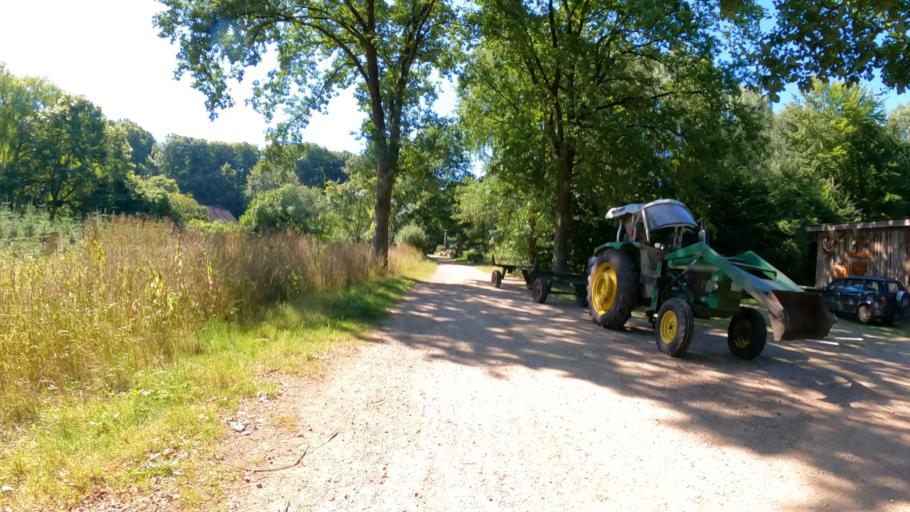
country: DE
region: Schleswig-Holstein
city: Kroppelshagen-Fahrendorf
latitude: 53.4922
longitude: 10.3340
